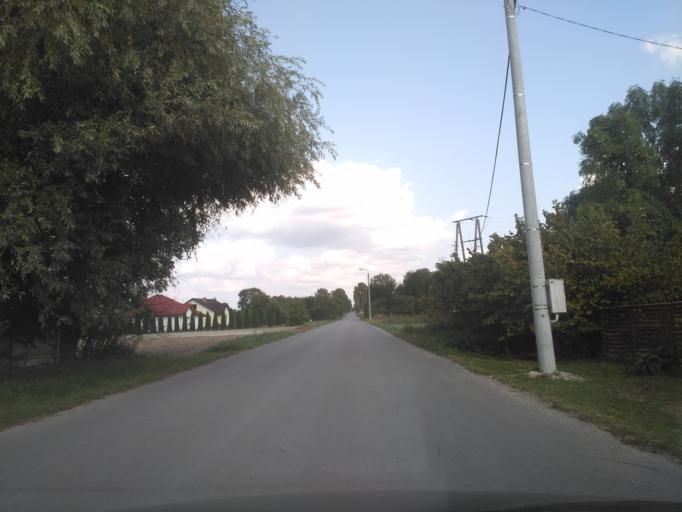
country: PL
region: Lublin Voivodeship
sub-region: Powiat chelmski
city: Pokrowka
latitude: 51.0677
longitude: 23.4856
